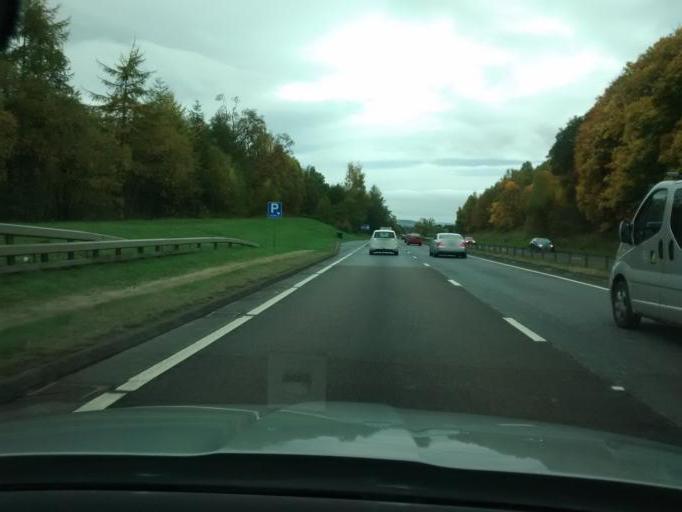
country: GB
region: Scotland
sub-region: Perth and Kinross
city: Luncarty
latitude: 56.4310
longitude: -3.4711
